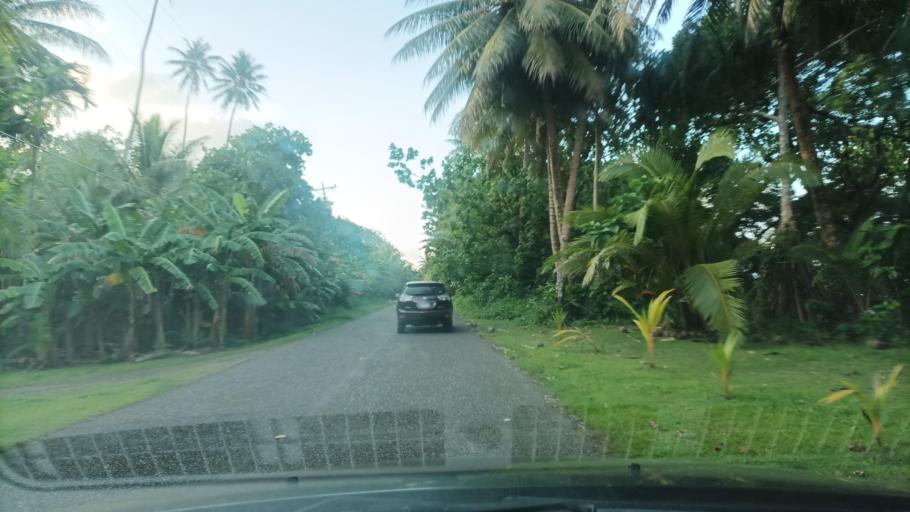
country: FM
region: Kosrae
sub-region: Lelu Municipality
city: Lelu
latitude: 5.3185
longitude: 163.0331
